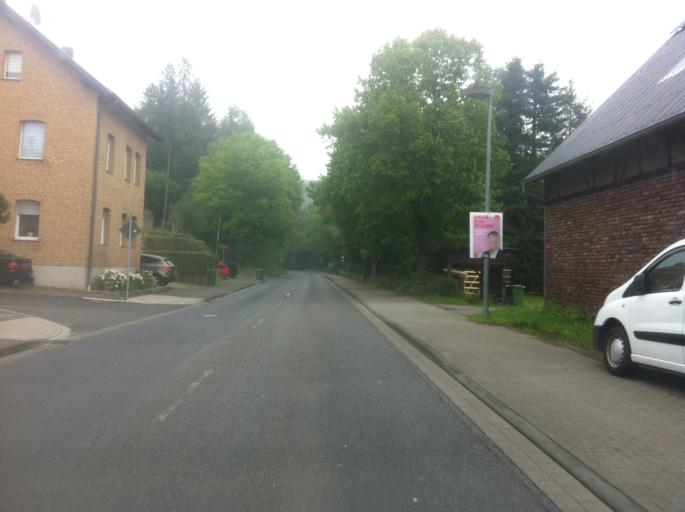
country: DE
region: North Rhine-Westphalia
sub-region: Regierungsbezirk Koln
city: Hennef
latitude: 50.7915
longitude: 7.3300
